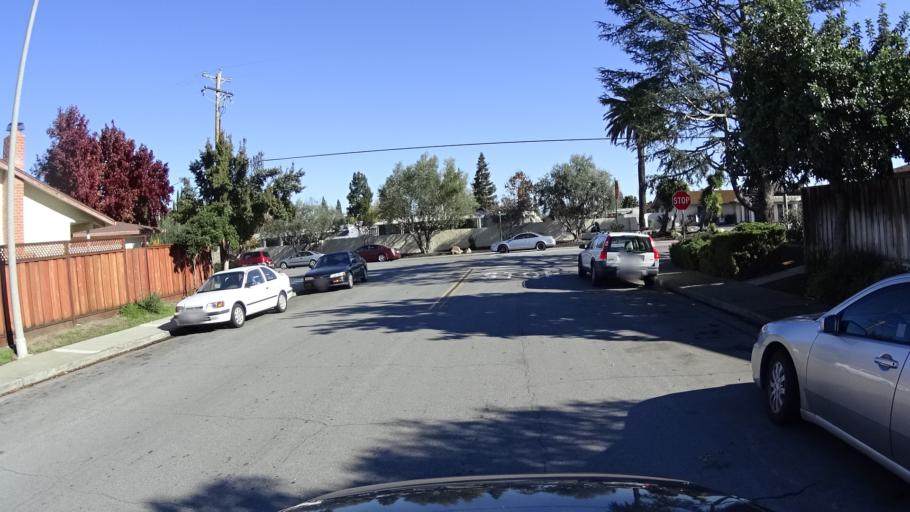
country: US
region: California
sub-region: Santa Clara County
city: Sunnyvale
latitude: 37.3585
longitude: -122.0055
